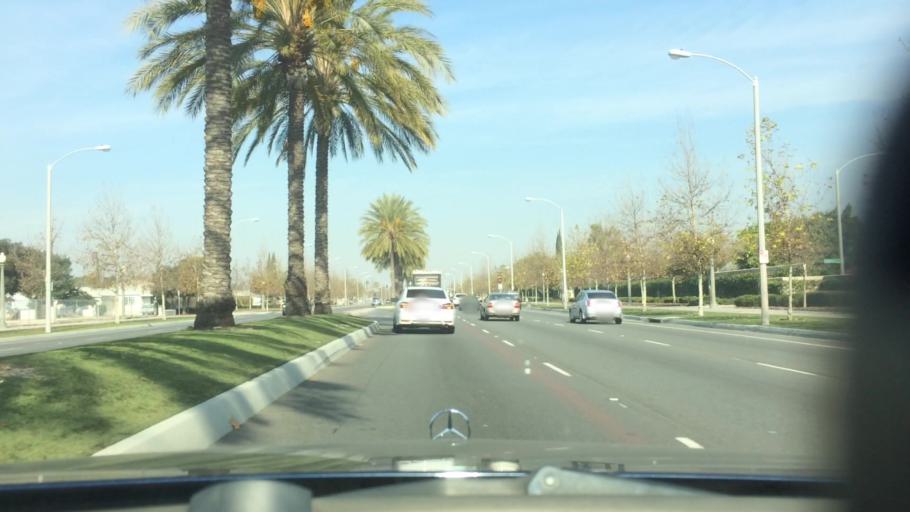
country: US
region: California
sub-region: Orange County
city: Santa Ana
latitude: 33.7369
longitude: -117.8851
